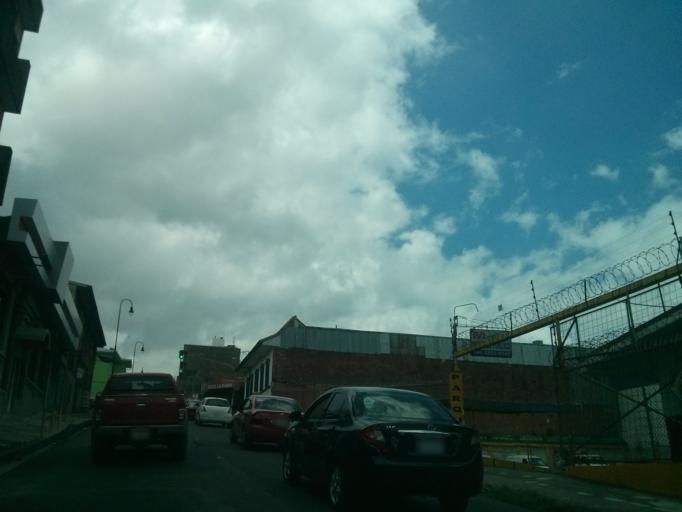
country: CR
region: San Jose
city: San Jose
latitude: 9.9389
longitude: -84.0778
